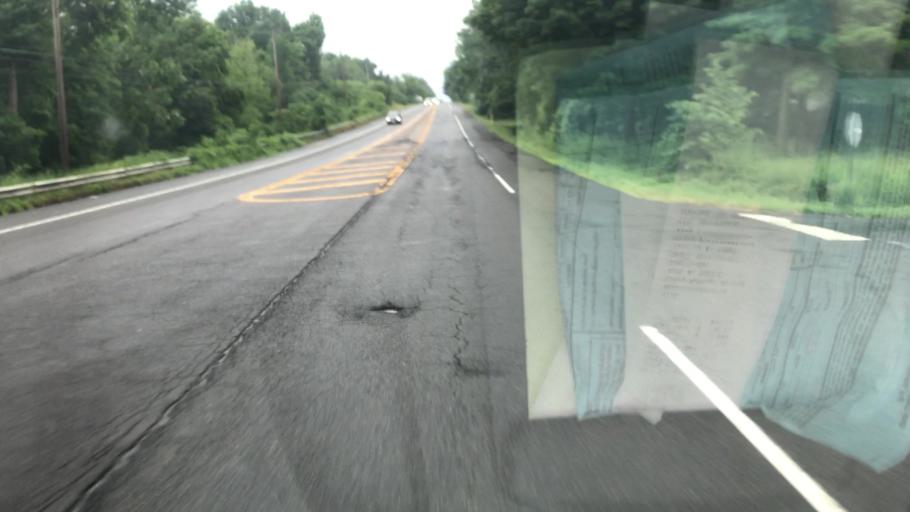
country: US
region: New York
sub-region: Onondaga County
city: Fayetteville
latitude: 43.0207
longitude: -76.0273
